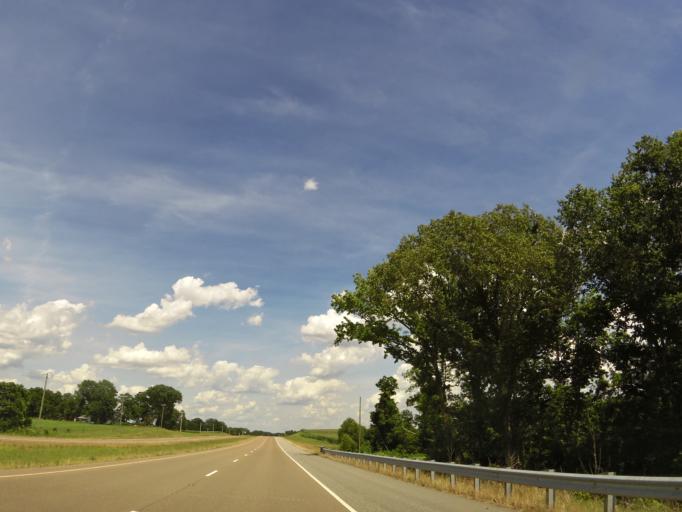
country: US
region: Tennessee
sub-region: Gibson County
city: Dyer
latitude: 35.9913
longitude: -89.0557
